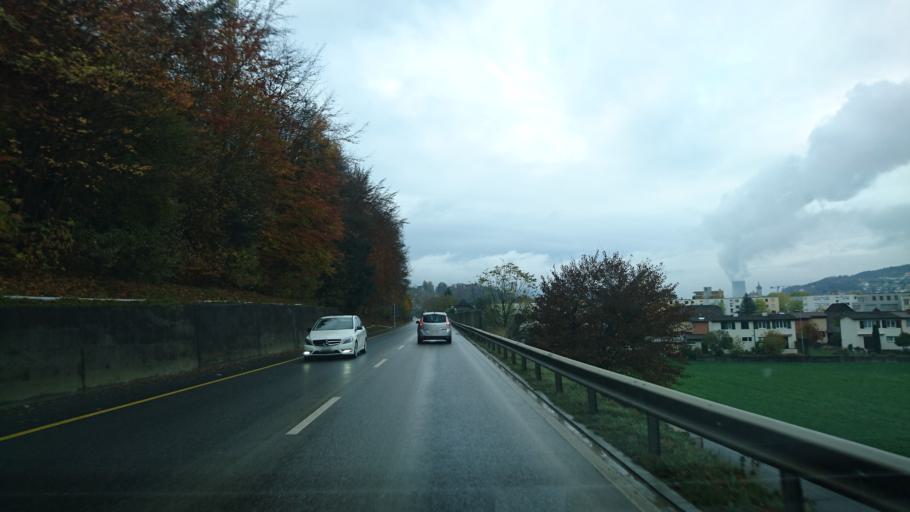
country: CH
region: Solothurn
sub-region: Bezirk Goesgen
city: Niedererlinsbach
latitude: 47.3790
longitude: 8.0155
